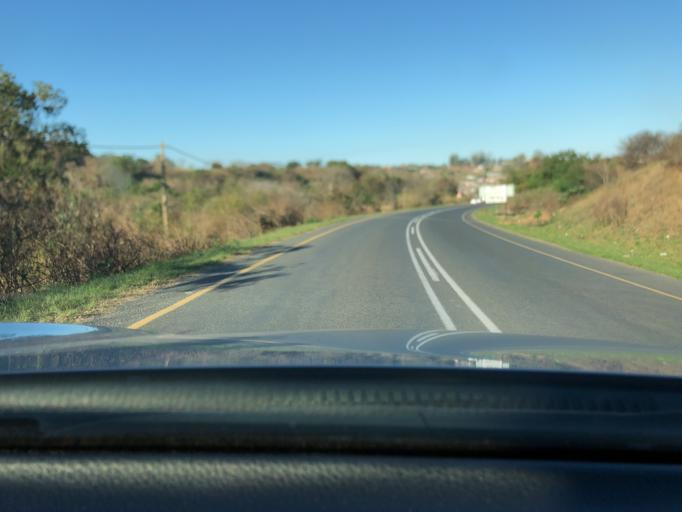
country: ZA
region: KwaZulu-Natal
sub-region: eThekwini Metropolitan Municipality
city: Umkomaas
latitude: -30.0351
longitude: 30.8120
